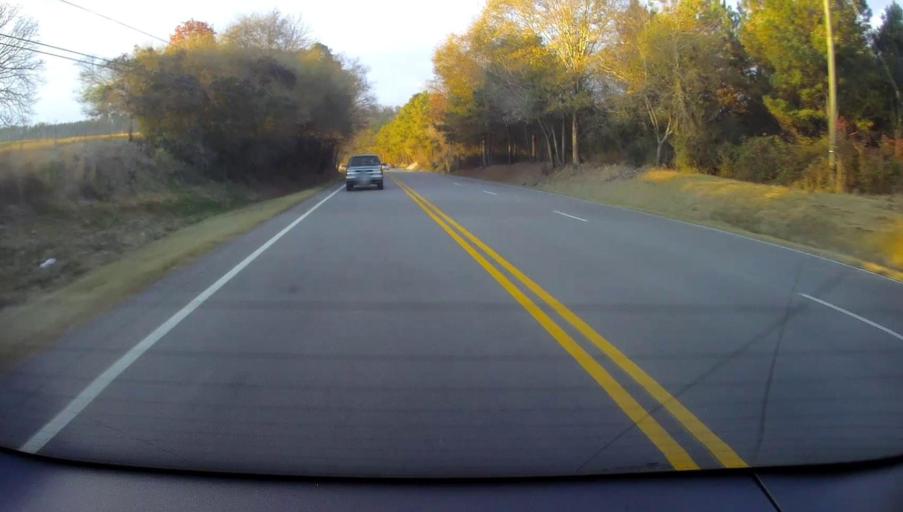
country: US
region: Alabama
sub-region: Etowah County
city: Attalla
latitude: 34.0492
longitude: -86.1594
